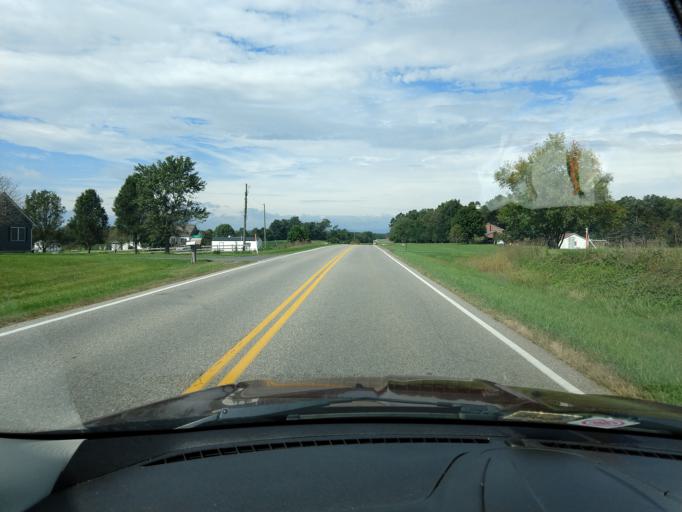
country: US
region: Virginia
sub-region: Augusta County
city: Weyers Cave
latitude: 38.2700
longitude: -78.8798
